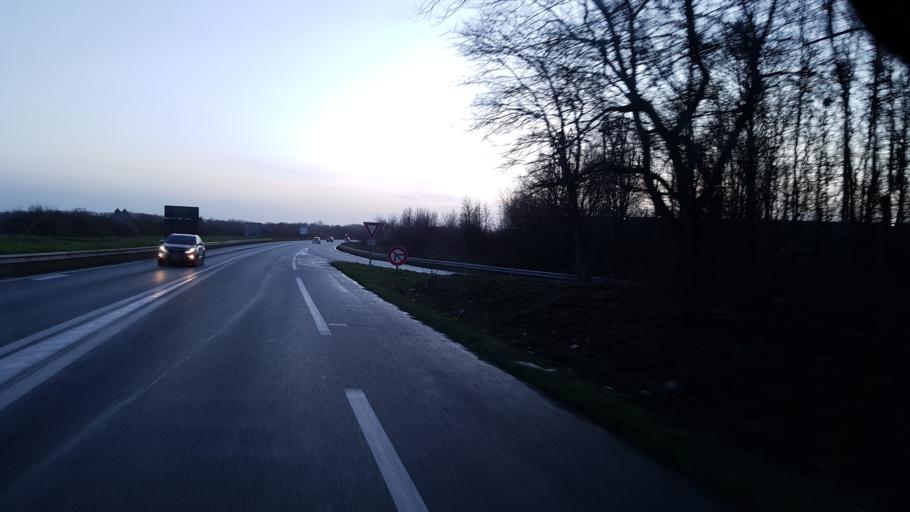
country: FR
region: Nord-Pas-de-Calais
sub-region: Departement du Nord
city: Lauwin-Planque
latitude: 50.3974
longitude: 3.0405
